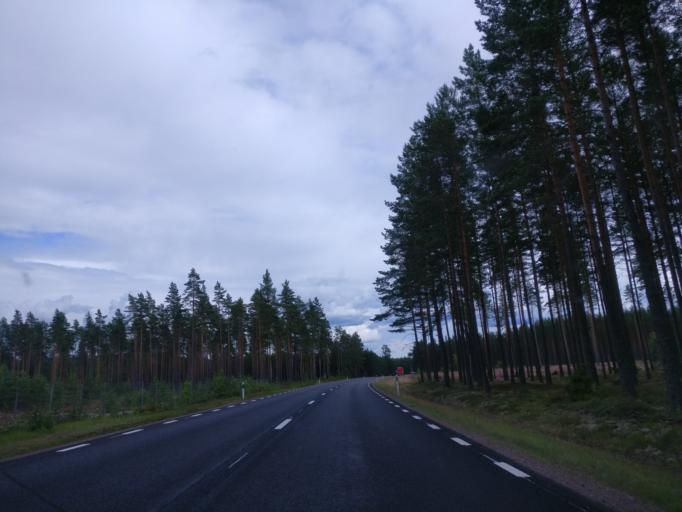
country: SE
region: Vaermland
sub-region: Hagfors Kommun
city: Hagfors
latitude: 60.0462
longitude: 13.5771
